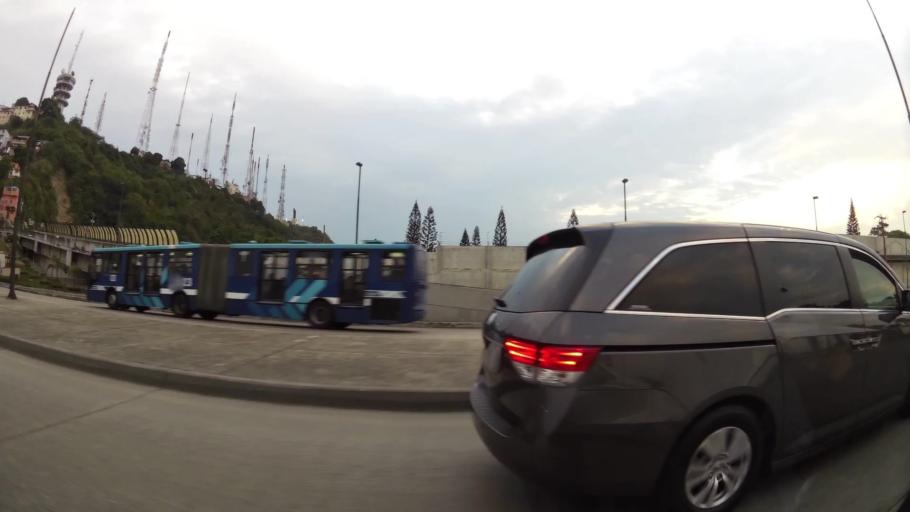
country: EC
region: Guayas
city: Eloy Alfaro
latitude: -2.1777
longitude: -79.8785
